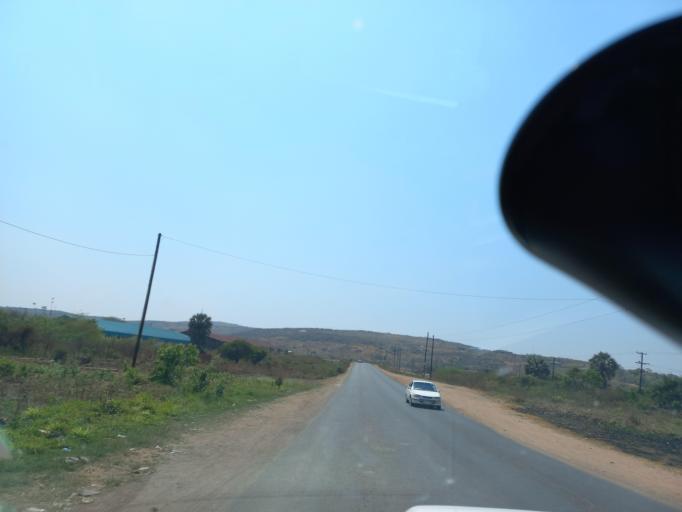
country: ZM
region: Lusaka
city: Kafue
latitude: -15.7589
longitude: 28.1762
